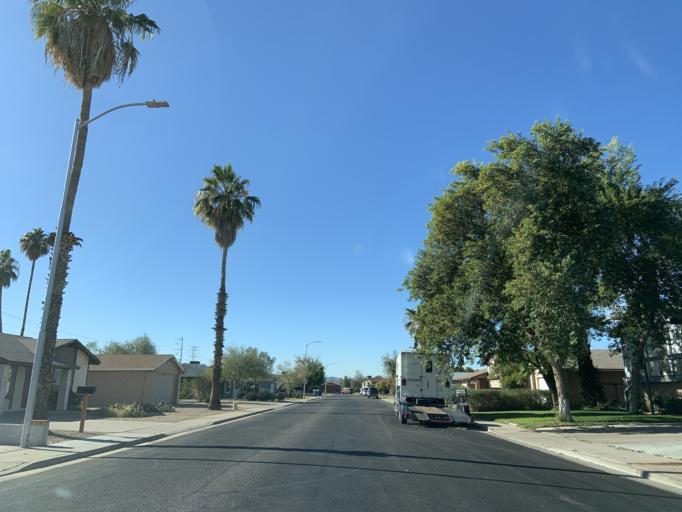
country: US
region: Arizona
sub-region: Maricopa County
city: San Carlos
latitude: 33.3581
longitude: -111.8687
